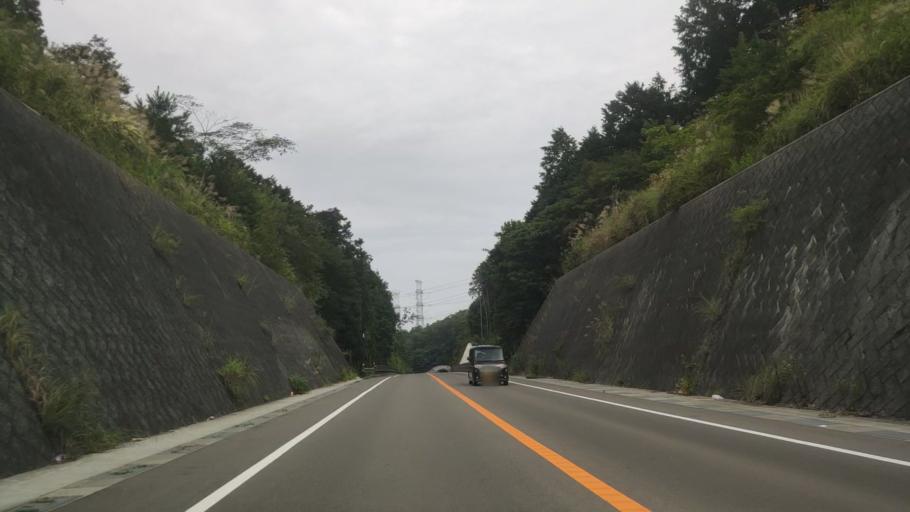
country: JP
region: Wakayama
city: Hashimoto
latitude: 34.4002
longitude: 135.5954
